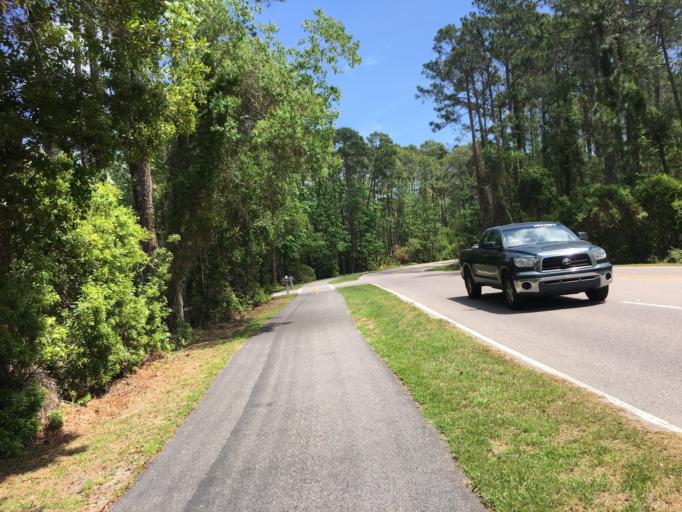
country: US
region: South Carolina
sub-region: Beaufort County
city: Hilton Head Island
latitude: 32.1695
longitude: -80.7722
